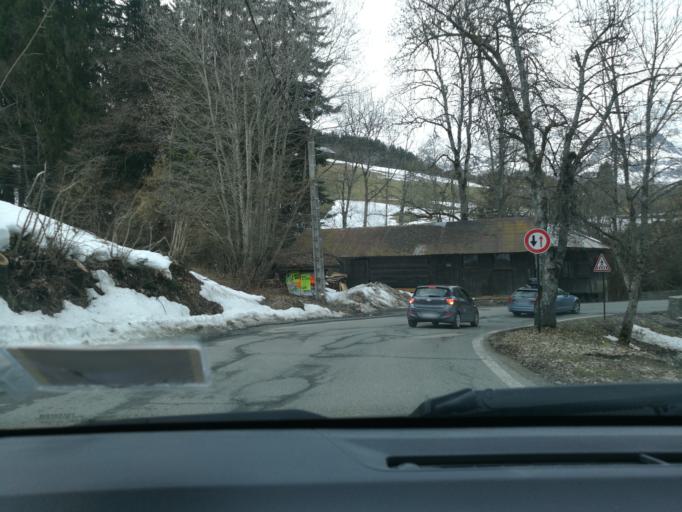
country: FR
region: Rhone-Alpes
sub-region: Departement de la Haute-Savoie
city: Combloux
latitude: 45.9045
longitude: 6.6340
